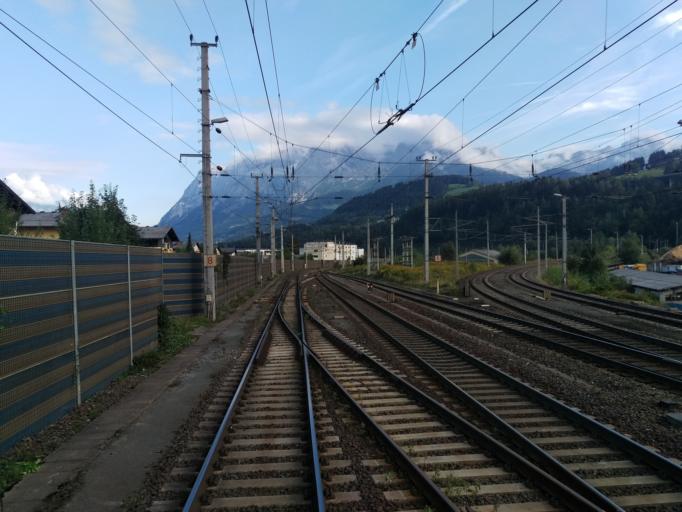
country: AT
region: Salzburg
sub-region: Politischer Bezirk Sankt Johann im Pongau
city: Bischofshofen
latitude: 47.4217
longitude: 13.2197
